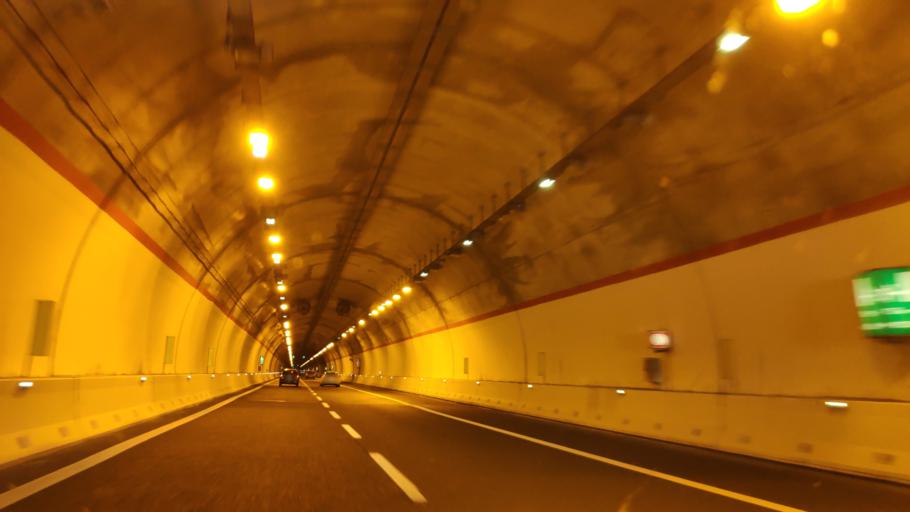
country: IT
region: Campania
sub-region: Provincia di Salerno
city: Casalbuono
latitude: 40.2017
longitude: 15.6859
